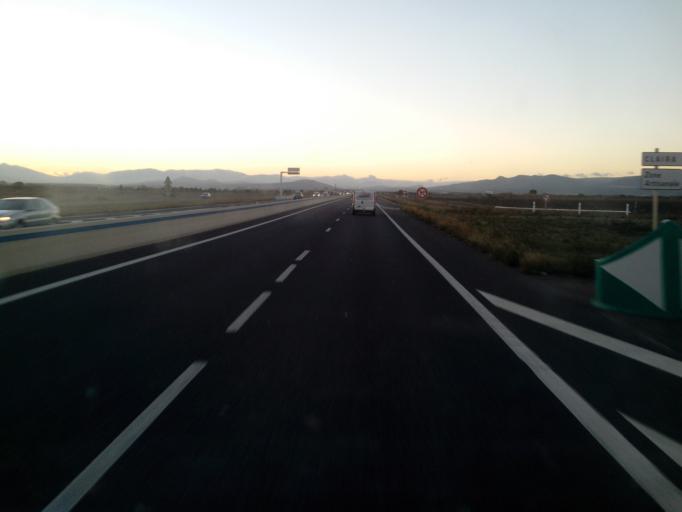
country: FR
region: Languedoc-Roussillon
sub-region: Departement des Pyrenees-Orientales
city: Claira
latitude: 42.7775
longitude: 2.9434
